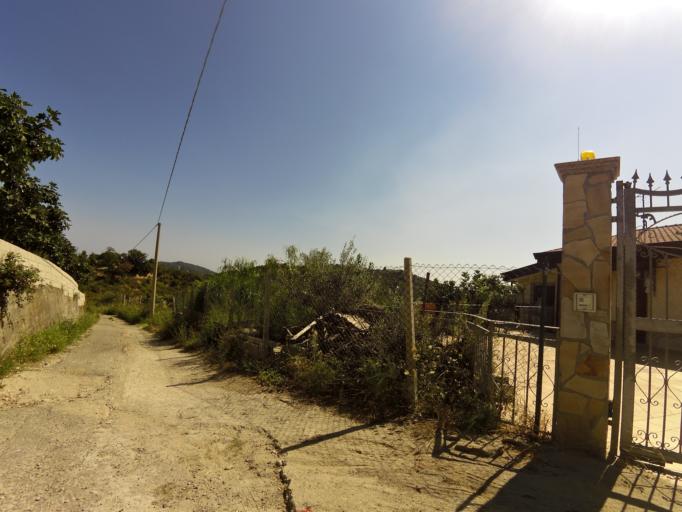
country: IT
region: Calabria
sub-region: Provincia di Reggio Calabria
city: Pazzano
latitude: 38.4607
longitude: 16.4550
